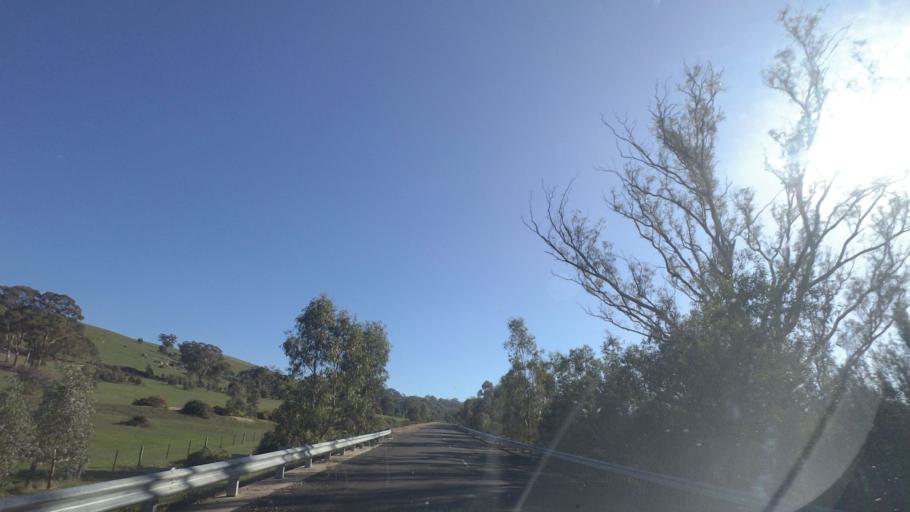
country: AU
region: Victoria
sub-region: Mount Alexander
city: Castlemaine
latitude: -37.0470
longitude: 144.2846
